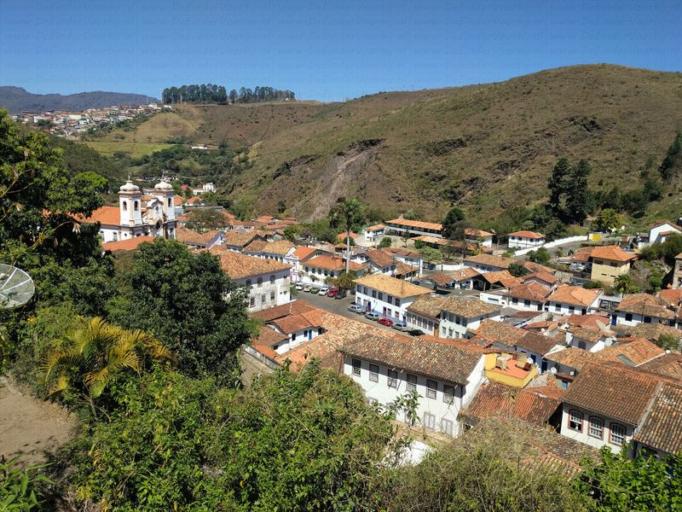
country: BR
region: Minas Gerais
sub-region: Ouro Preto
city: Ouro Preto
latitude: -20.3852
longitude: -43.5082
